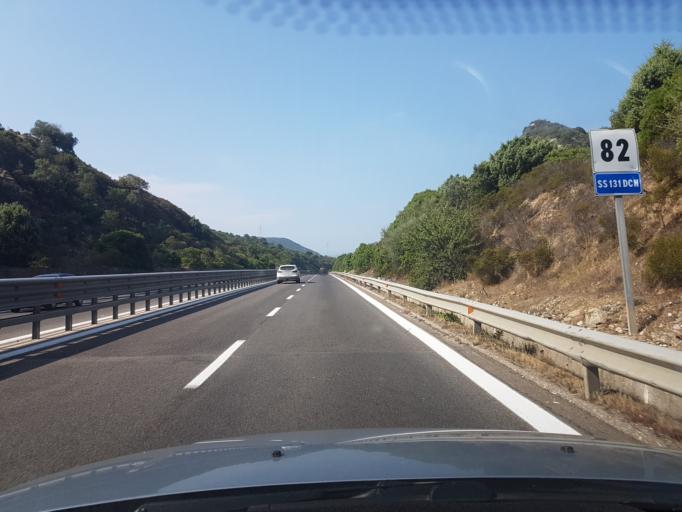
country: IT
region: Sardinia
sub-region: Provincia di Nuoro
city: Loculi
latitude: 40.4699
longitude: 9.5836
